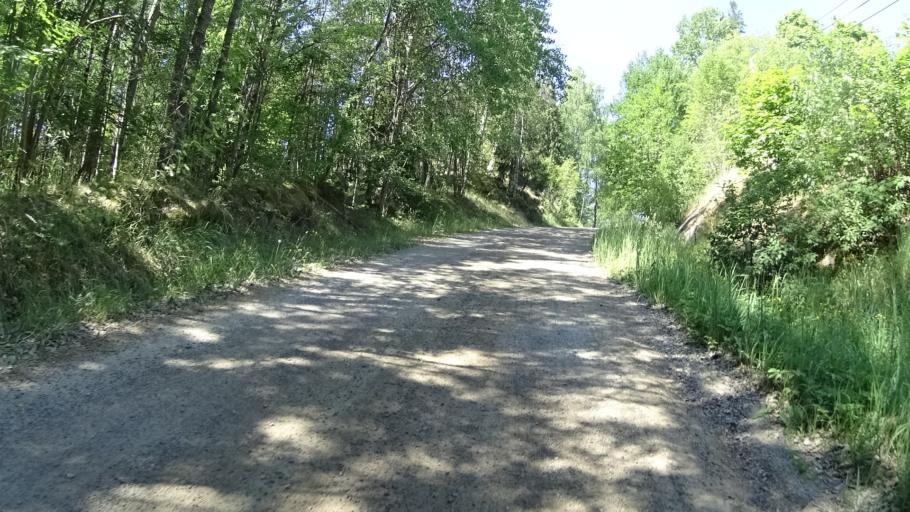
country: FI
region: Uusimaa
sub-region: Raaseporin
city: Pohja
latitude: 60.0950
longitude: 23.5650
